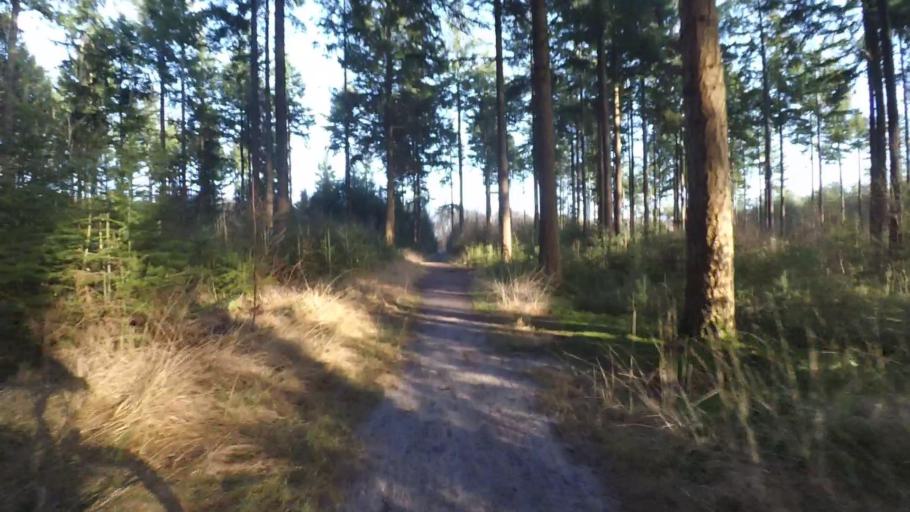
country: NL
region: Utrecht
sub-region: Gemeente Utrechtse Heuvelrug
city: Maarn
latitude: 52.0917
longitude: 5.3504
